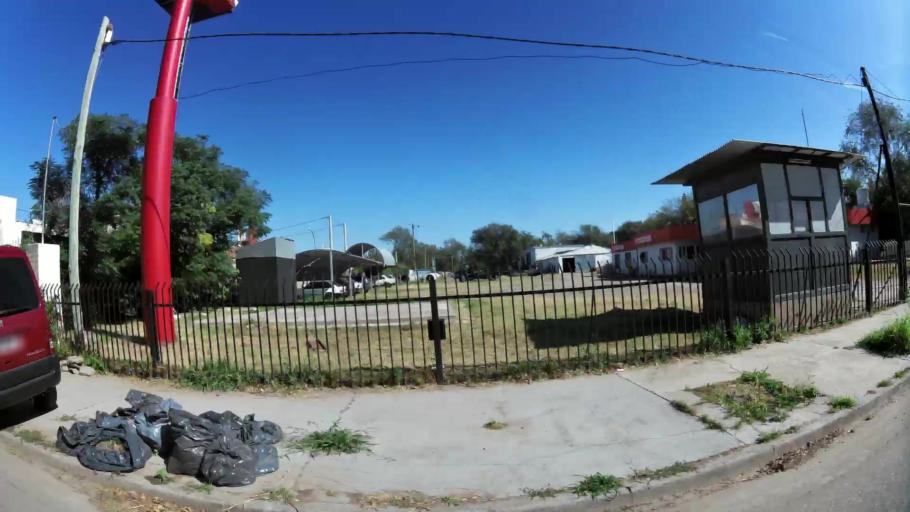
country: AR
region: Cordoba
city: Villa Allende
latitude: -31.3382
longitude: -64.2417
